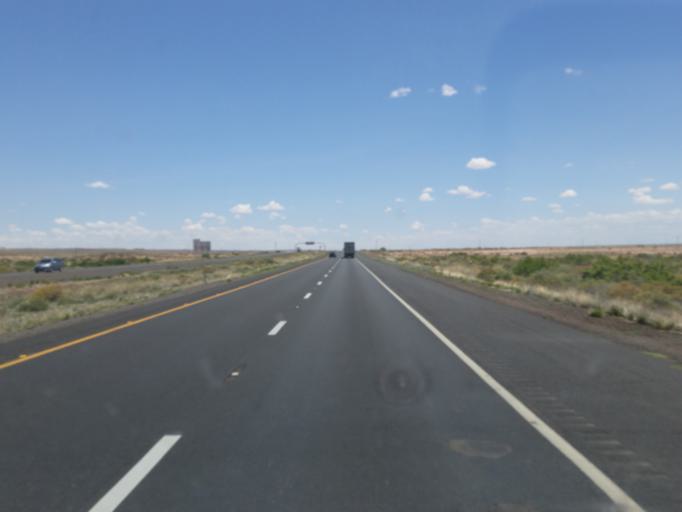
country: US
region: Arizona
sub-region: Navajo County
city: Winslow
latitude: 35.0027
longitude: -110.6065
